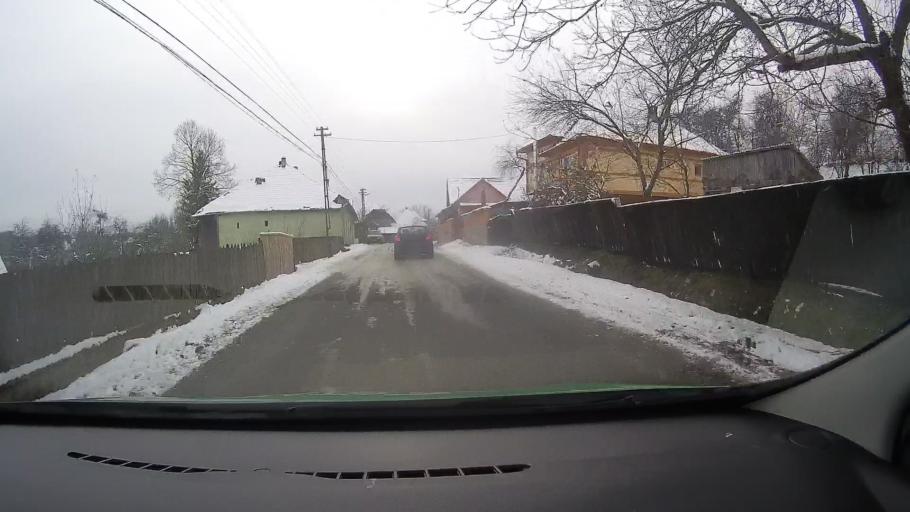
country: RO
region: Alba
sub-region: Comuna Almasu Mare
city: Almasu Mare
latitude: 46.0890
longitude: 23.1298
